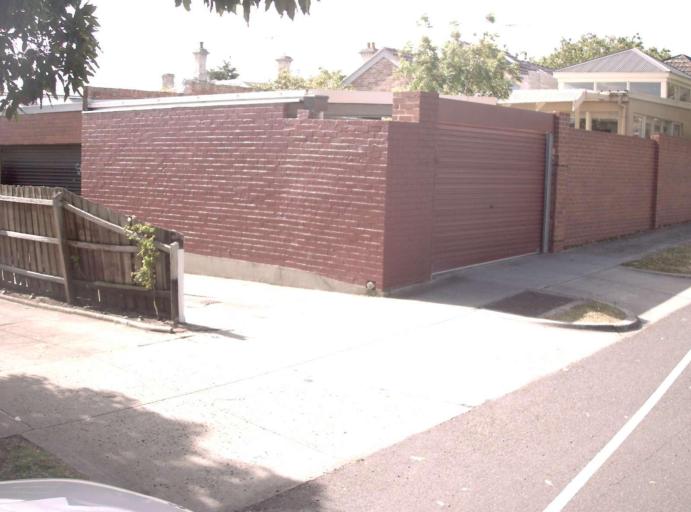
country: AU
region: Victoria
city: Glenferrie
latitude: -37.8311
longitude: 145.0476
